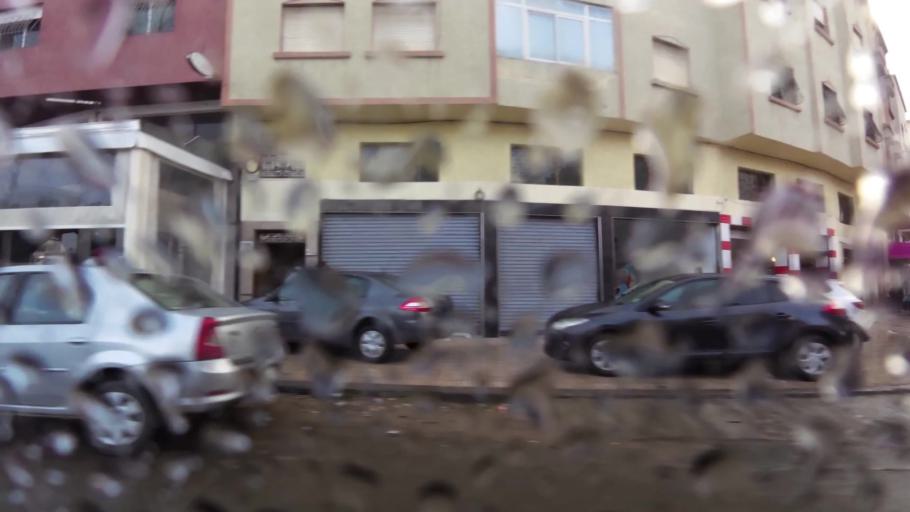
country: MA
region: Doukkala-Abda
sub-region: El-Jadida
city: El Jadida
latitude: 33.2449
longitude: -8.5240
